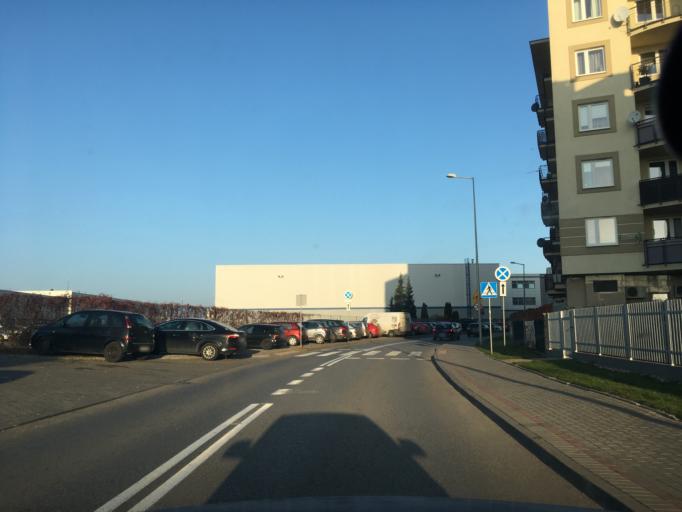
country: PL
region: Masovian Voivodeship
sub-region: Powiat piaseczynski
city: Piaseczno
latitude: 52.0782
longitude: 21.0086
